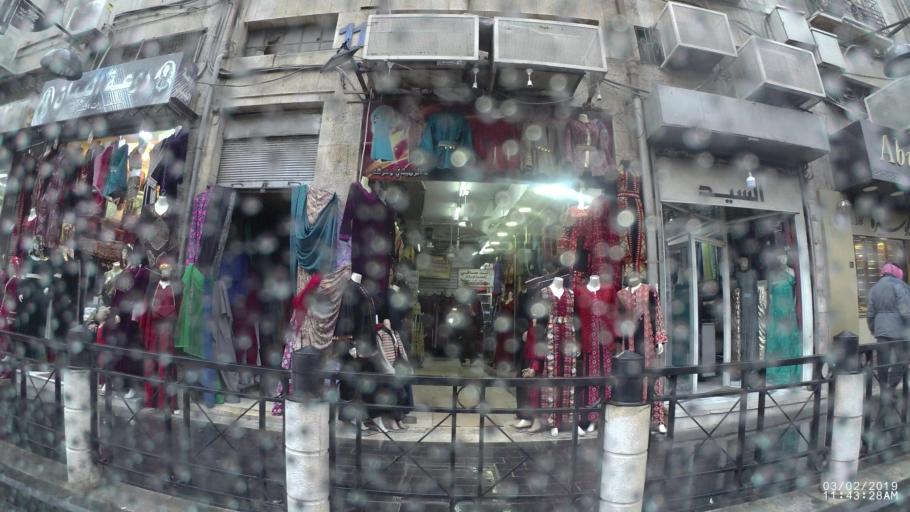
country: JO
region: Amman
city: Amman
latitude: 31.9510
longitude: 35.9346
